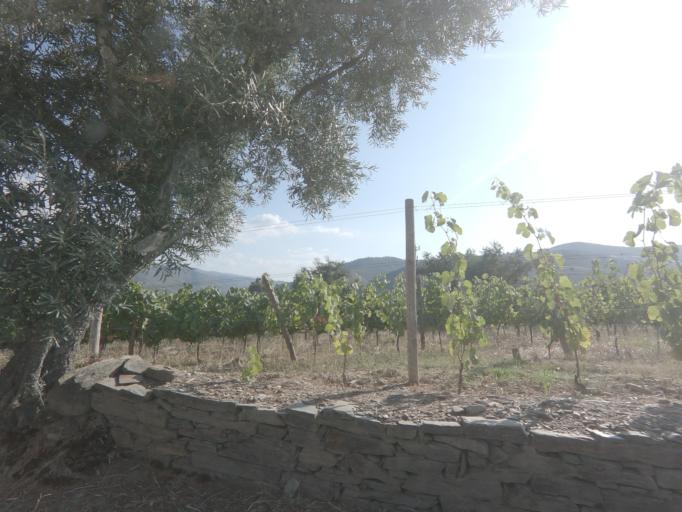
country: PT
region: Vila Real
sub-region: Sabrosa
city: Vilela
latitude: 41.1948
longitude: -7.5429
